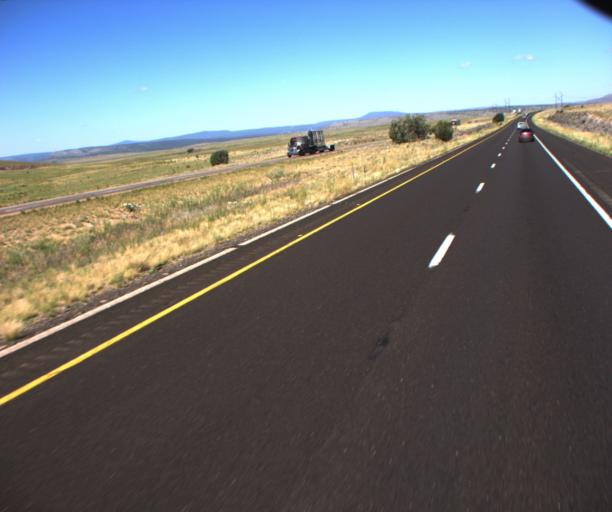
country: US
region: Arizona
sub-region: Yavapai County
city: Paulden
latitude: 35.2874
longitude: -112.8088
